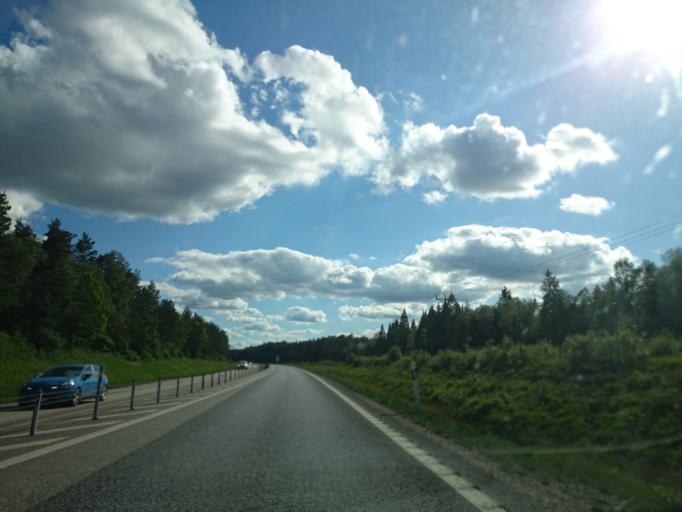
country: SE
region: Kronoberg
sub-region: Ljungby Kommun
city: Ljungby
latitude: 56.8402
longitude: 13.9179
